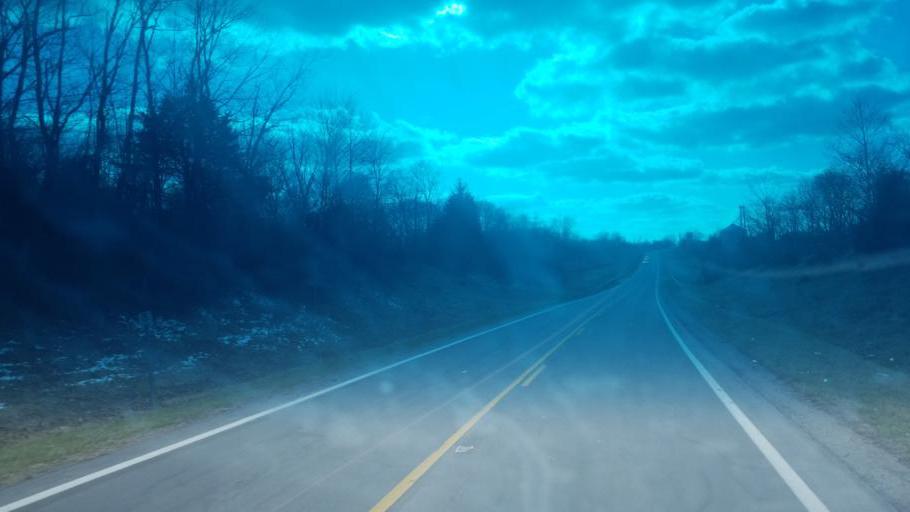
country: US
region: Ohio
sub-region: Highland County
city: Greenfield
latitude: 39.3463
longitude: -83.4118
